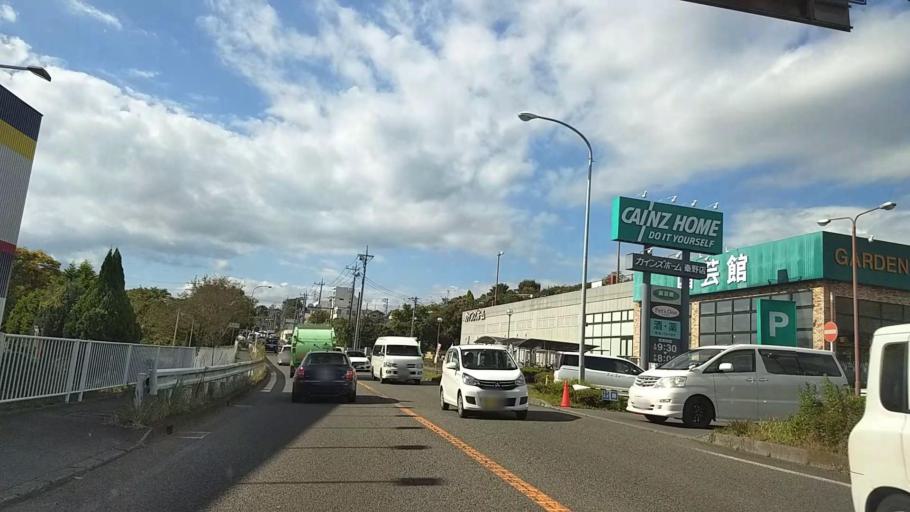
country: JP
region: Kanagawa
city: Hadano
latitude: 35.3813
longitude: 139.2288
